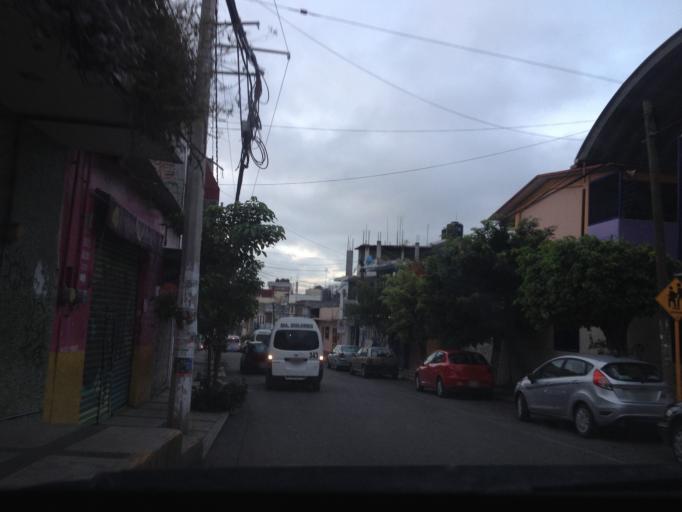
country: MX
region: Guerrero
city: Chilpancingo de los Bravos
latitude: 17.5499
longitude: -99.5012
